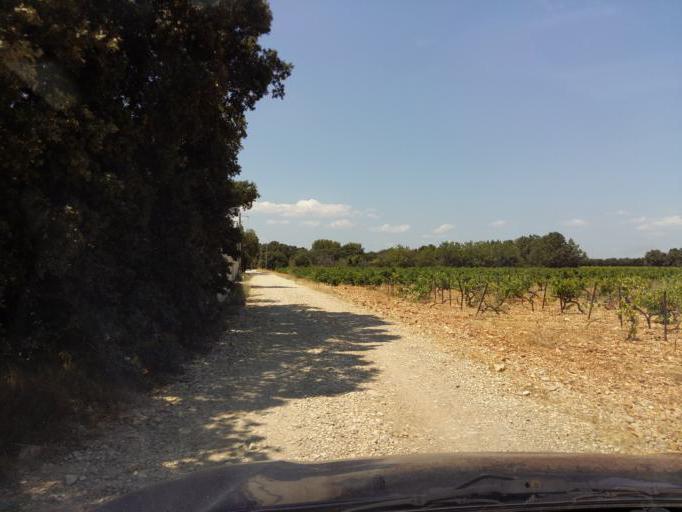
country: FR
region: Provence-Alpes-Cote d'Azur
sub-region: Departement du Vaucluse
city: Camaret-sur-Aigues
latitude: 44.1795
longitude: 4.8619
